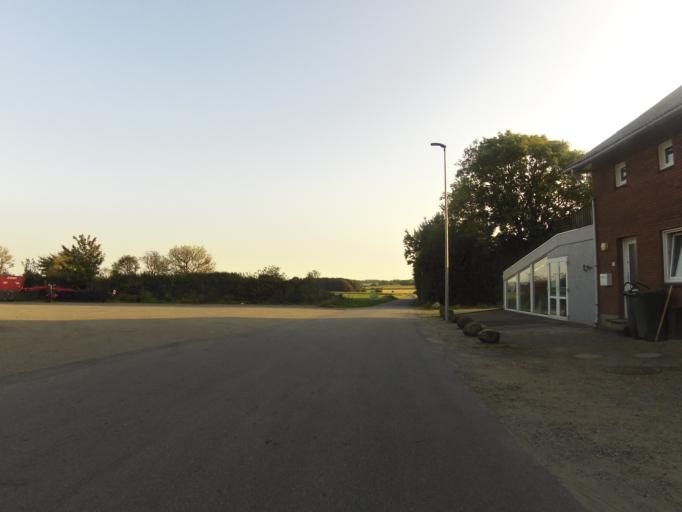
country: DK
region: South Denmark
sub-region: Vejen Kommune
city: Rodding
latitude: 55.3459
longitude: 9.1299
